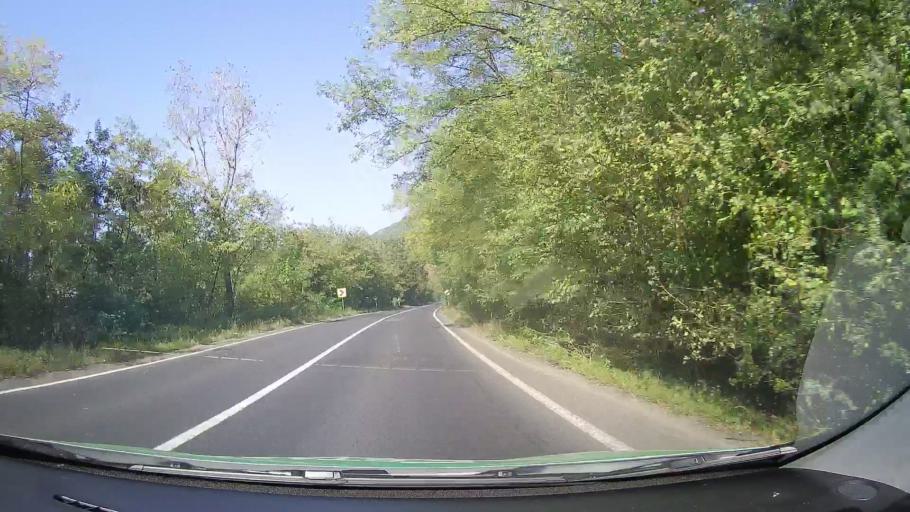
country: RO
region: Arad
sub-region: Comuna Savarsin
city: Savarsin
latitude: 46.0047
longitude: 22.2758
